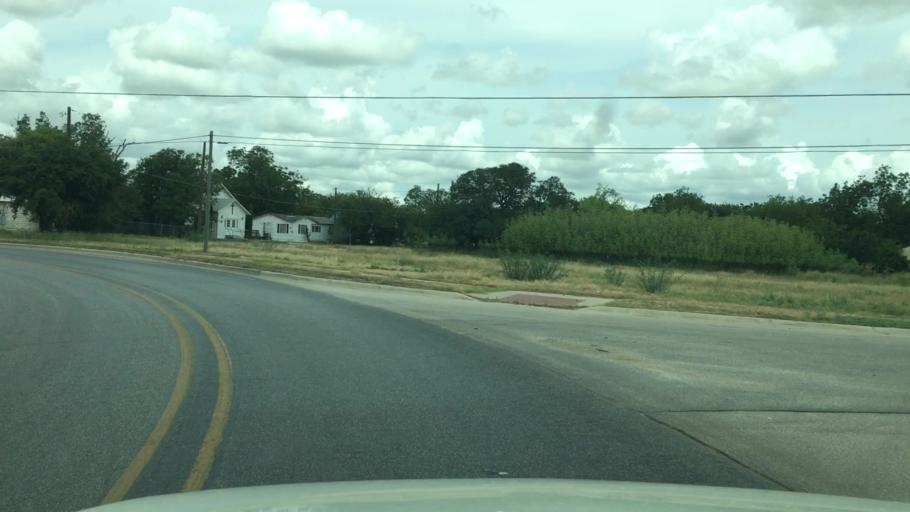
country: US
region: Texas
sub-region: McCulloch County
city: Brady
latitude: 31.1259
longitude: -99.3268
